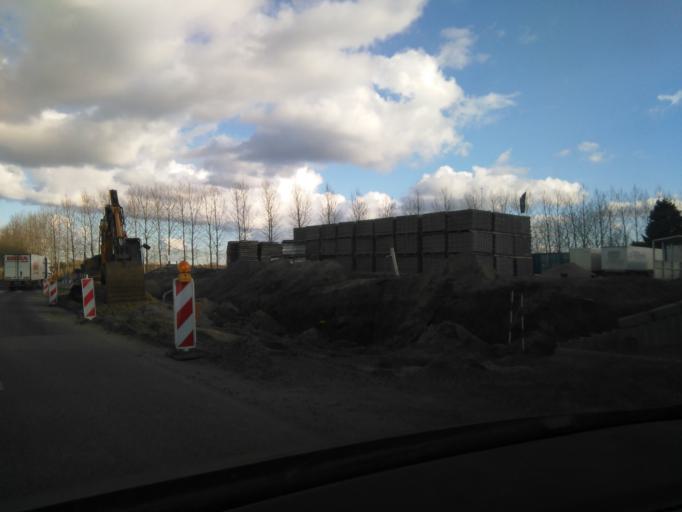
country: DK
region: Central Jutland
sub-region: Silkeborg Kommune
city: Silkeborg
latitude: 56.1867
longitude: 9.5079
